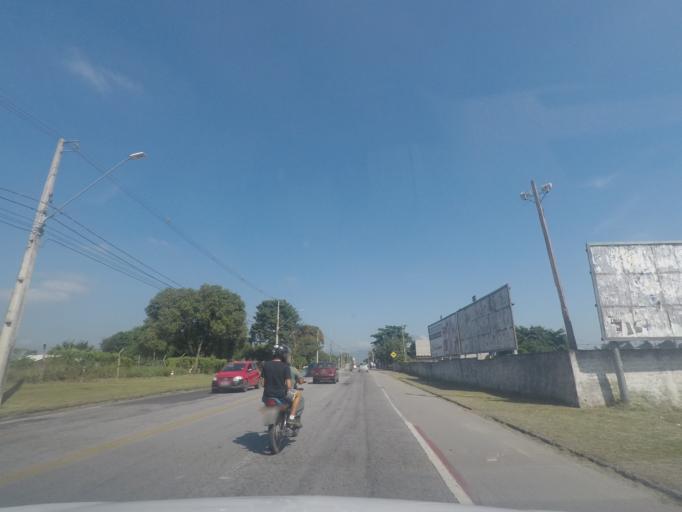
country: BR
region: Parana
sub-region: Paranagua
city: Paranagua
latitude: -25.5409
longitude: -48.5352
